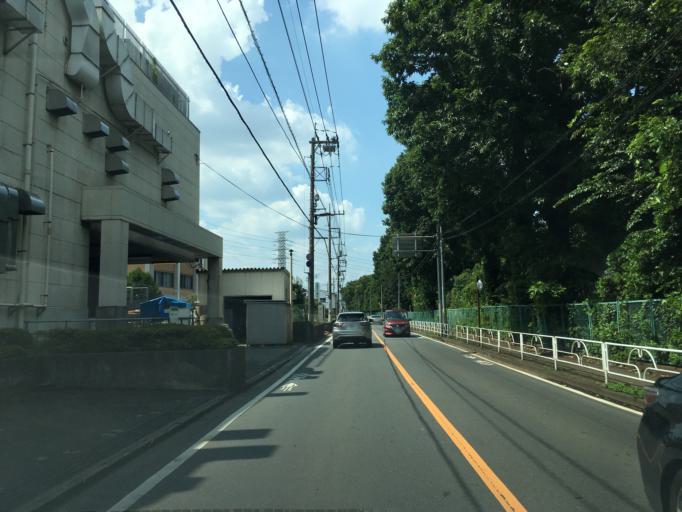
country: JP
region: Tokyo
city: Higashimurayama-shi
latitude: 35.7643
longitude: 139.4941
